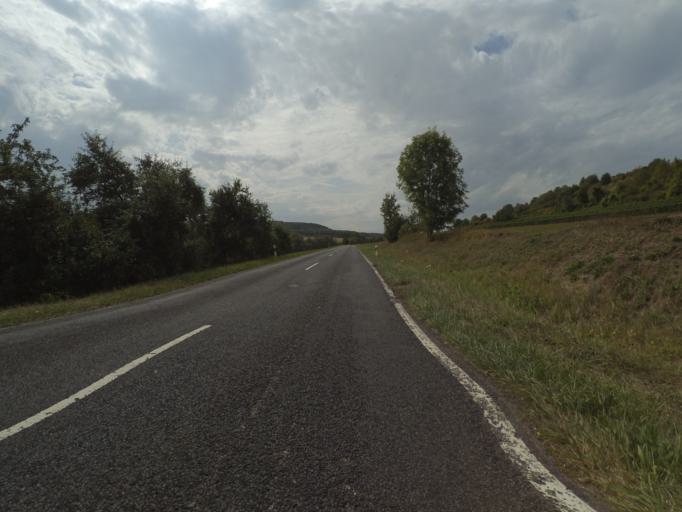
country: DE
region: Rheinland-Pfalz
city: Onsdorf
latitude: 49.6557
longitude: 6.4917
